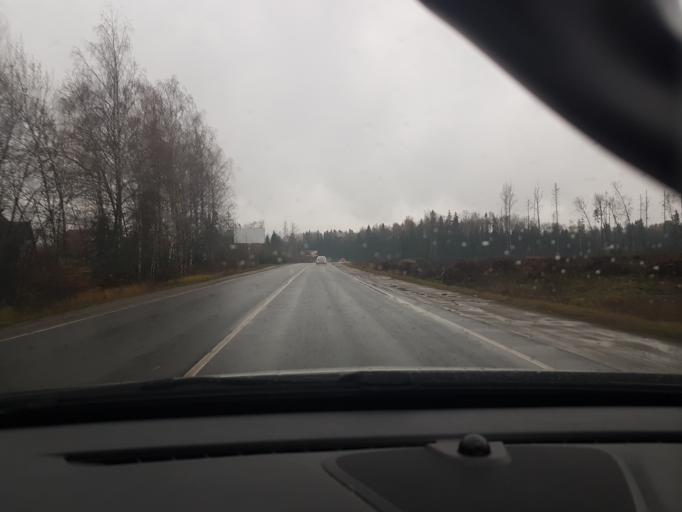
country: RU
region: Moskovskaya
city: Rozhdestveno
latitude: 55.8352
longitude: 37.0173
